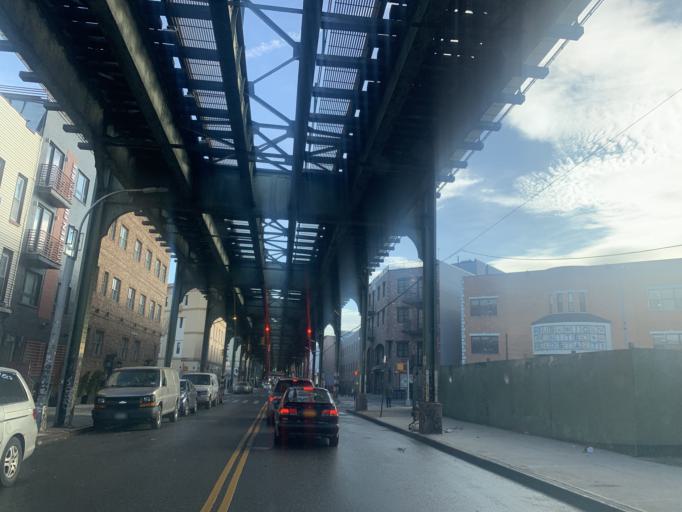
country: US
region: New York
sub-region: Kings County
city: East New York
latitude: 40.6982
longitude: -73.9240
